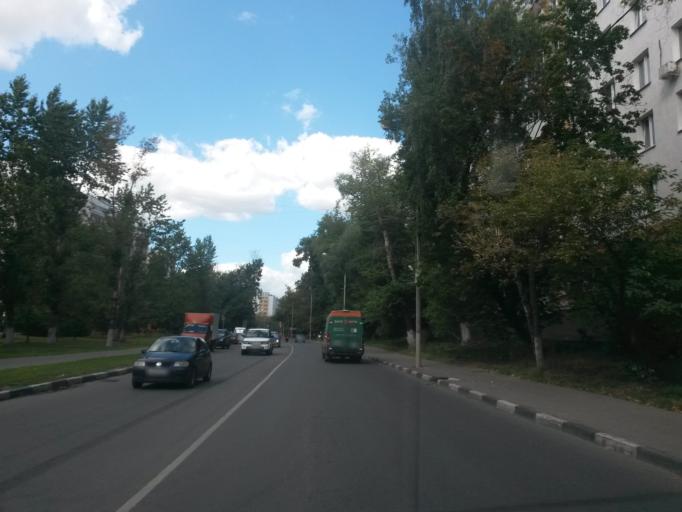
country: RU
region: Moscow
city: Tekstil'shchiki
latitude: 55.6832
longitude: 37.7243
